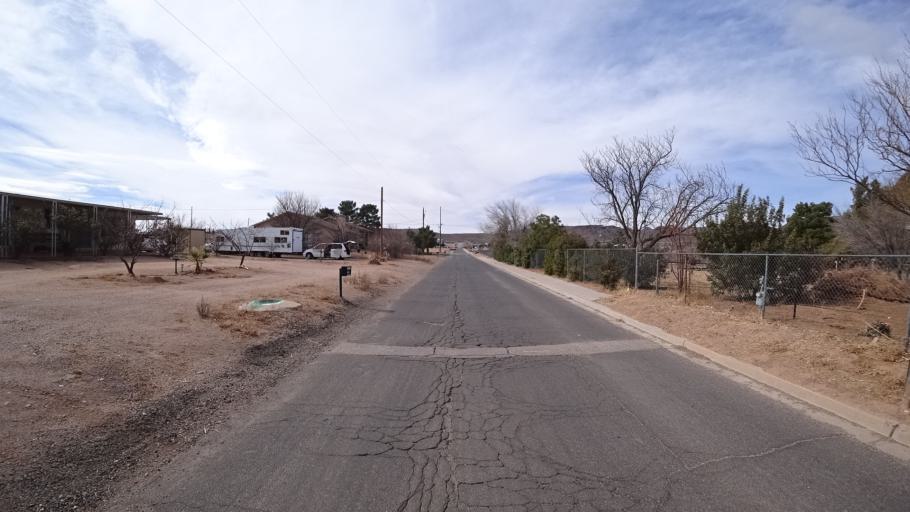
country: US
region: Arizona
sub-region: Mohave County
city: New Kingman-Butler
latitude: 35.2286
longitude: -114.0321
